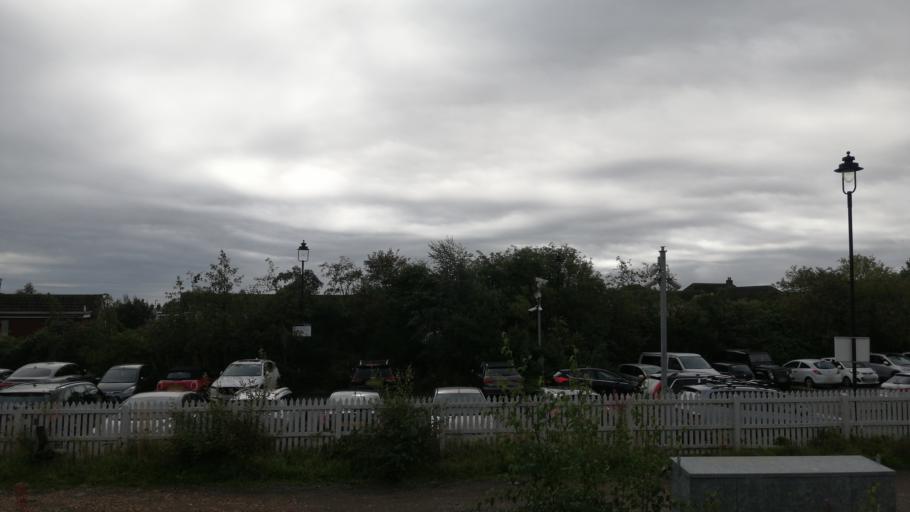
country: GB
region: Scotland
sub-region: Aberdeenshire
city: Stonehaven
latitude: 56.9676
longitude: -2.2237
